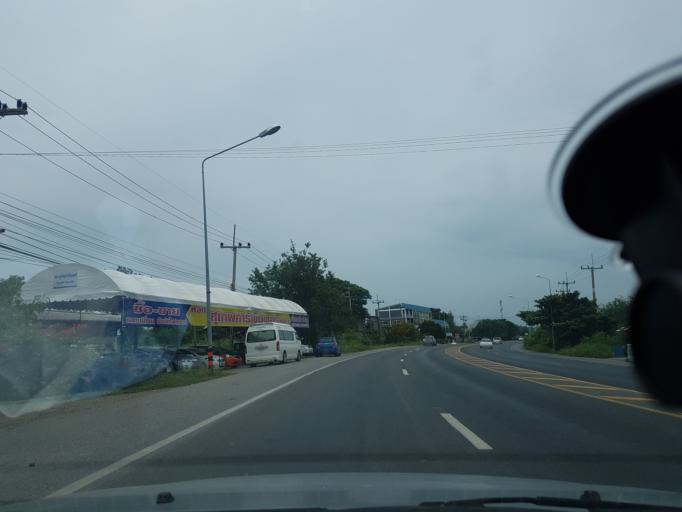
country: TH
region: Lop Buri
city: Lop Buri
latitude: 14.8100
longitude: 100.5944
